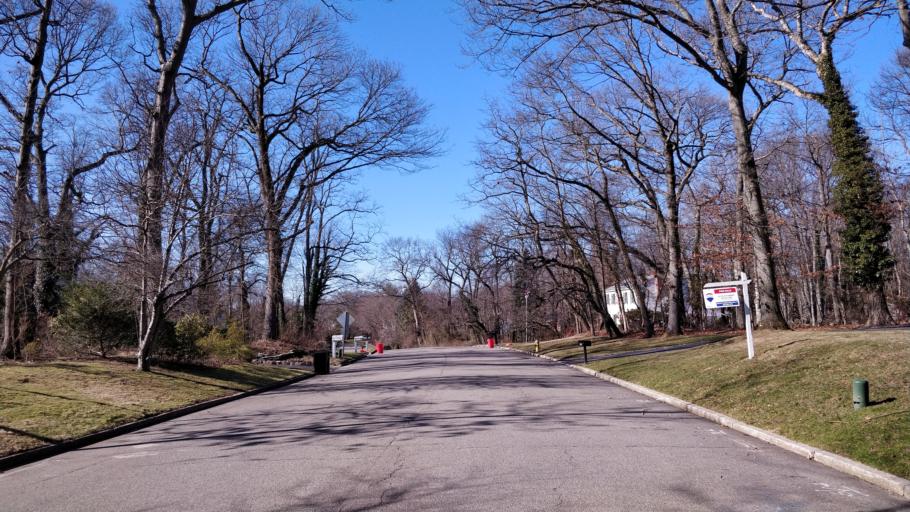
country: US
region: New York
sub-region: Suffolk County
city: Port Jefferson
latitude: 40.9372
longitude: -73.0802
